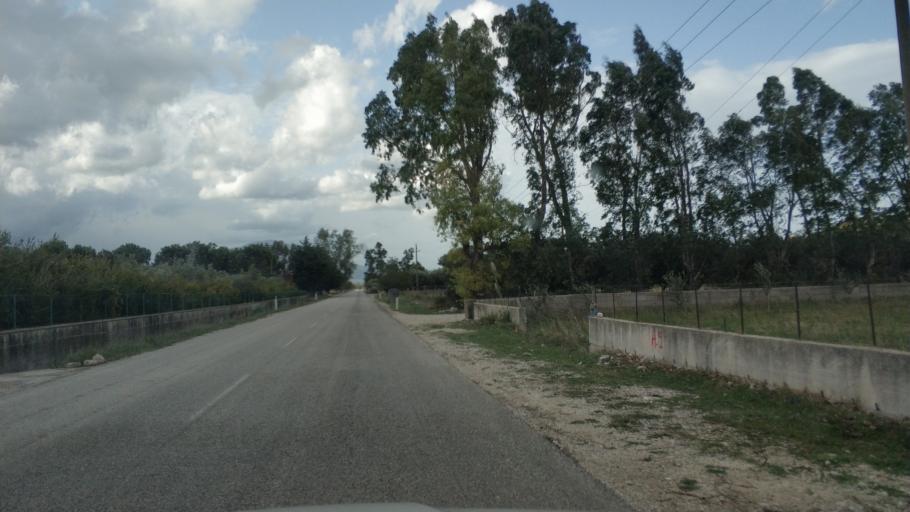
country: AL
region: Vlore
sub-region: Rrethi i Vlores
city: Orikum
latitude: 40.2824
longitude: 19.5002
